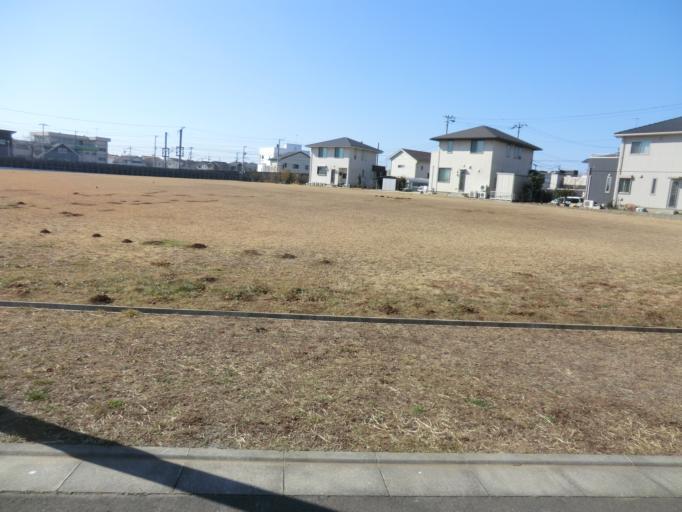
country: JP
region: Ibaraki
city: Naka
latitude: 36.0810
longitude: 140.0964
